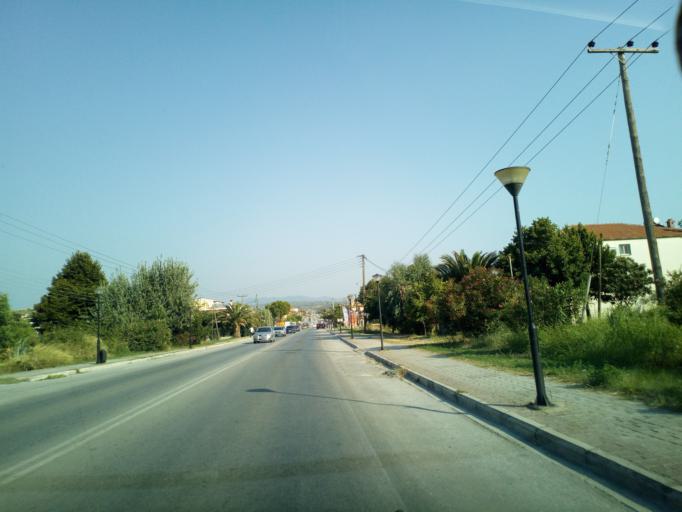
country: GR
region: Central Macedonia
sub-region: Nomos Chalkidikis
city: Nikiti
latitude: 40.2254
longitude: 23.6648
